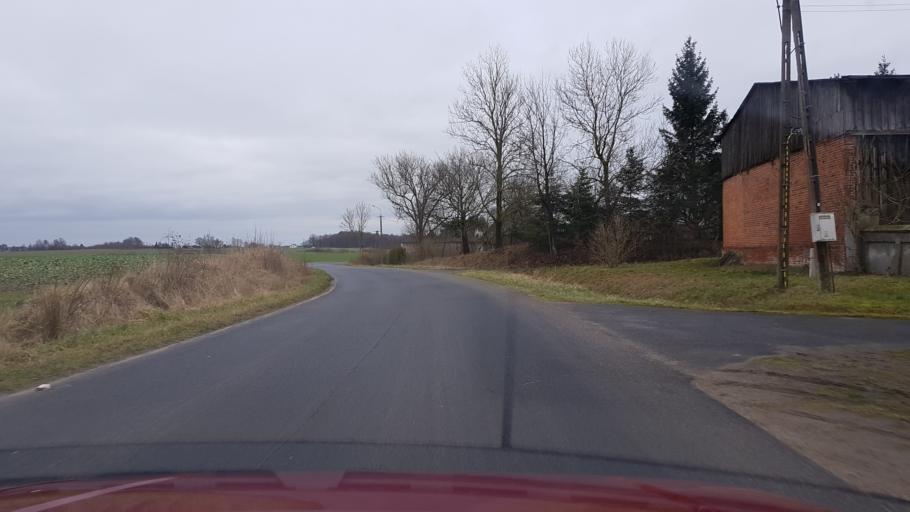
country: PL
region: West Pomeranian Voivodeship
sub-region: Powiat koszalinski
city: Mielno
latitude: 54.1782
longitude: 16.0107
